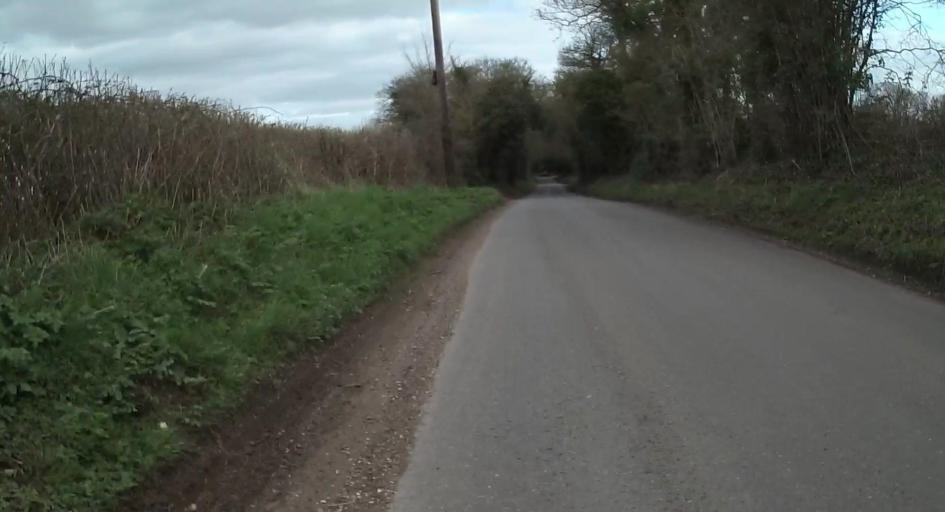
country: GB
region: England
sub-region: Hampshire
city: Andover
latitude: 51.1550
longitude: -1.4687
